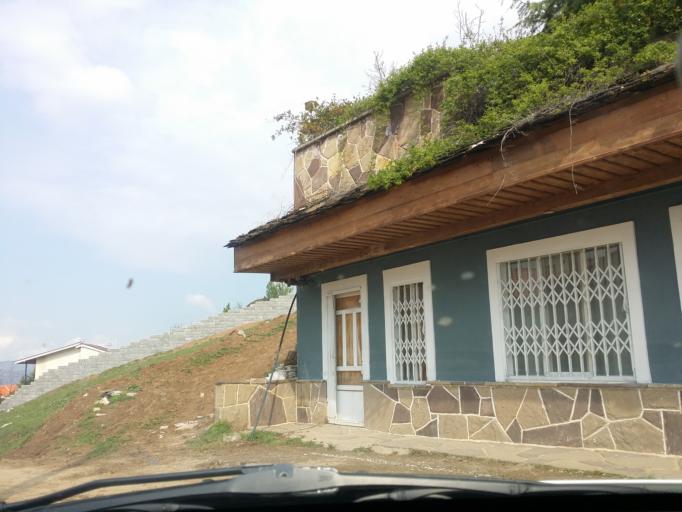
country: IR
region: Mazandaran
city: `Abbasabad
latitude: 36.4853
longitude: 51.1408
